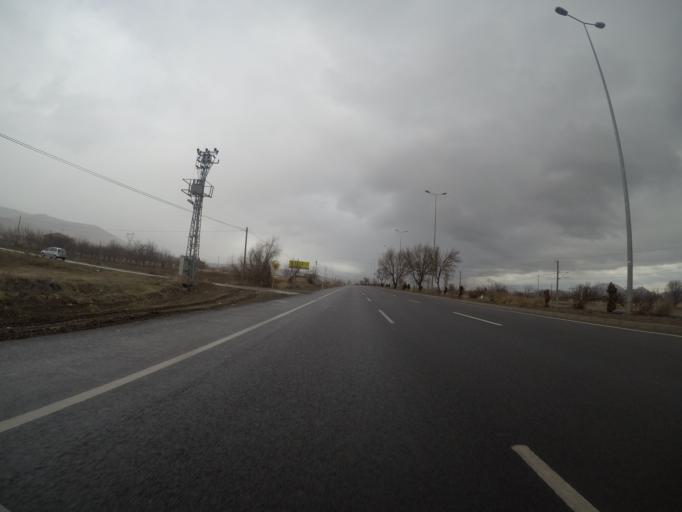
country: TR
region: Kayseri
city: Incesu
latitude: 38.6927
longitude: 35.2448
